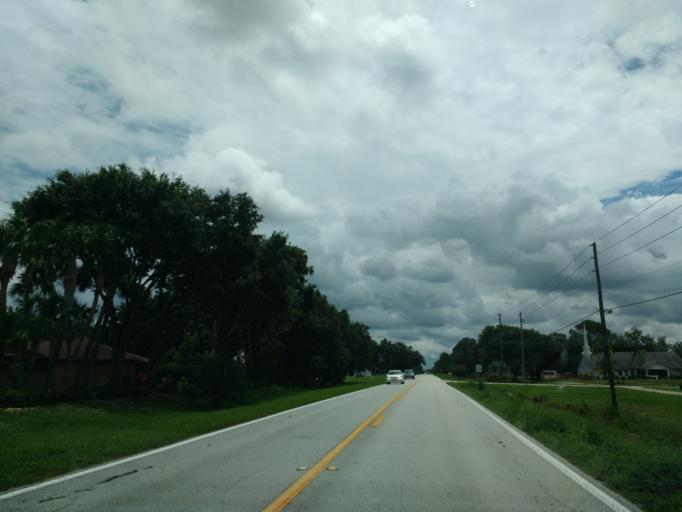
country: US
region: Florida
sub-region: Highlands County
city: Sebring
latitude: 27.4709
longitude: -81.5025
